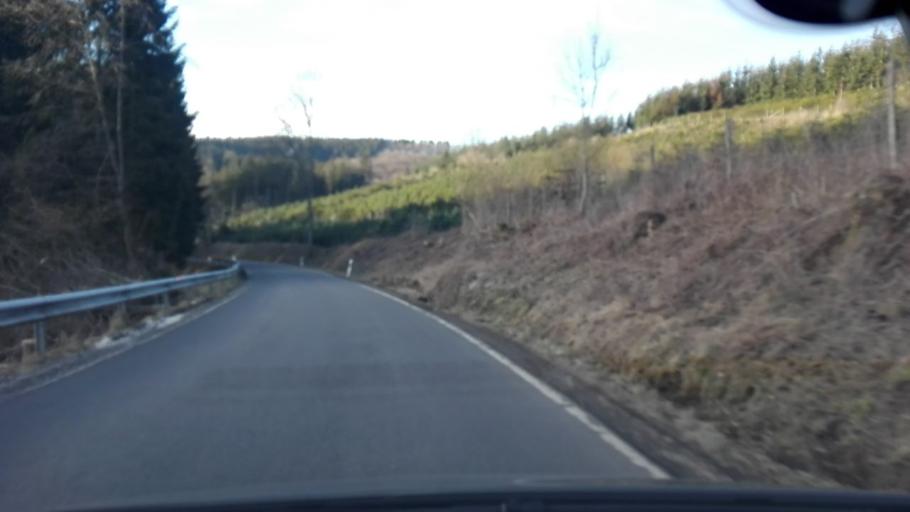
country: DE
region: North Rhine-Westphalia
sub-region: Regierungsbezirk Arnsberg
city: Kirchhundem
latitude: 51.1723
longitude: 8.1417
